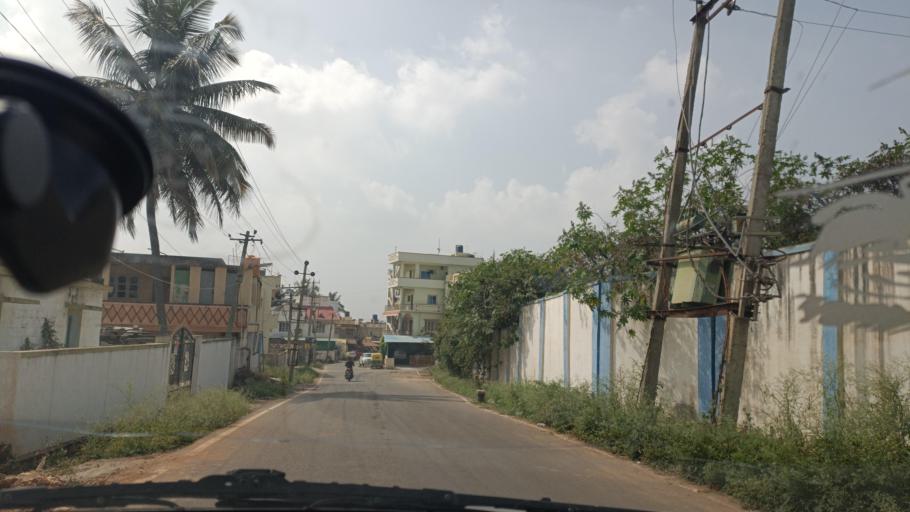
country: IN
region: Karnataka
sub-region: Bangalore Urban
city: Yelahanka
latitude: 13.1458
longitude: 77.6043
